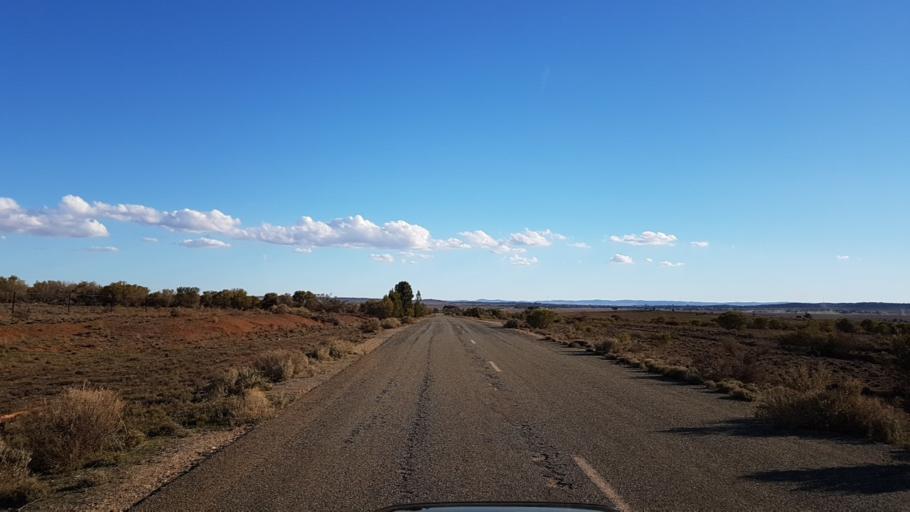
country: AU
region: South Australia
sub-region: Peterborough
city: Peterborough
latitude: -32.9573
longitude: 138.8982
